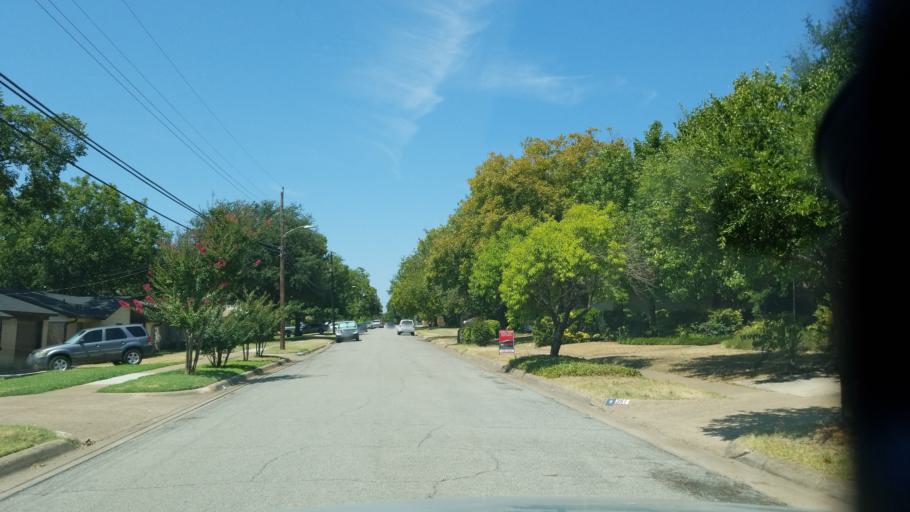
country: US
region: Texas
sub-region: Dallas County
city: Duncanville
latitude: 32.6526
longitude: -96.9030
